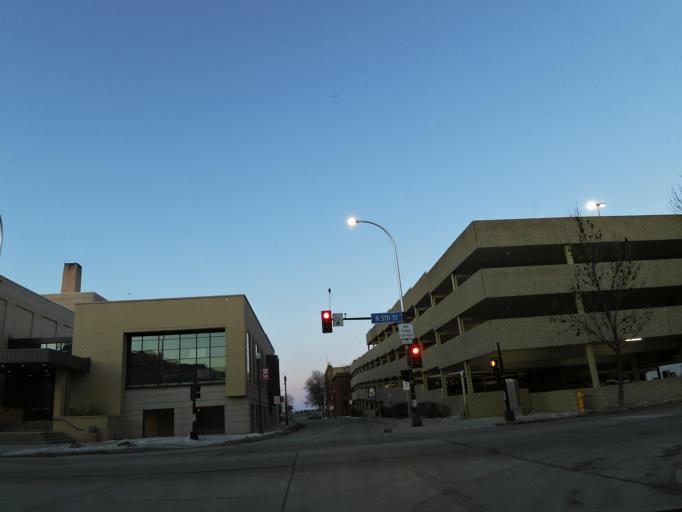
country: US
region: North Dakota
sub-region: Grand Forks County
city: Grand Forks
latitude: 47.9242
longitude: -97.0338
